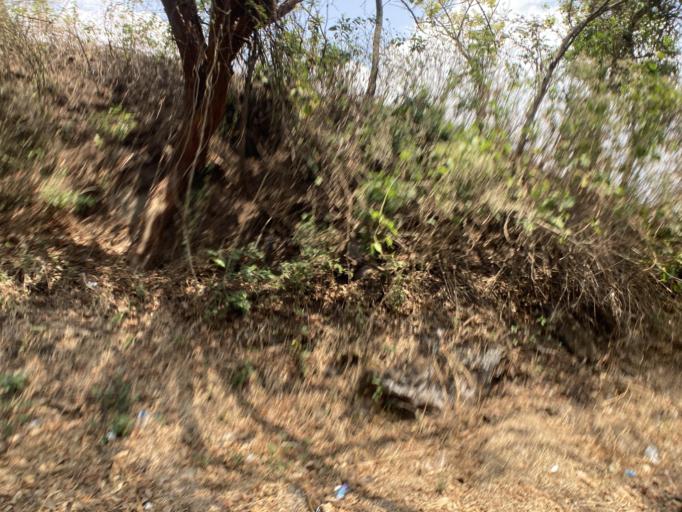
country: GT
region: Escuintla
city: San Vicente Pacaya
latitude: 14.3758
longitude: -90.5561
